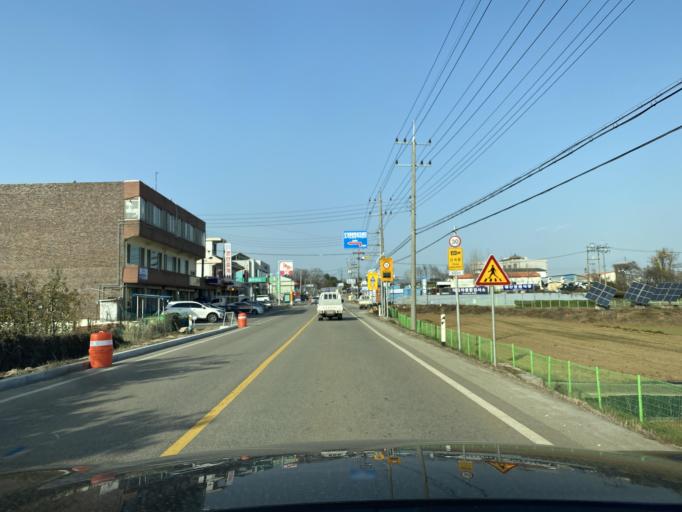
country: KR
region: Chungcheongnam-do
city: Yesan
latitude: 36.6870
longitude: 126.8000
